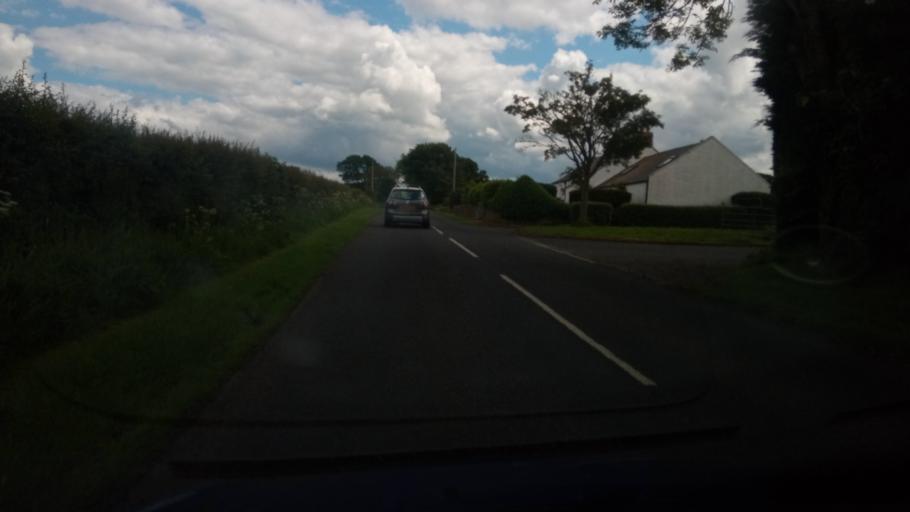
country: GB
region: Scotland
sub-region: The Scottish Borders
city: Coldstream
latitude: 55.6034
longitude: -2.2867
